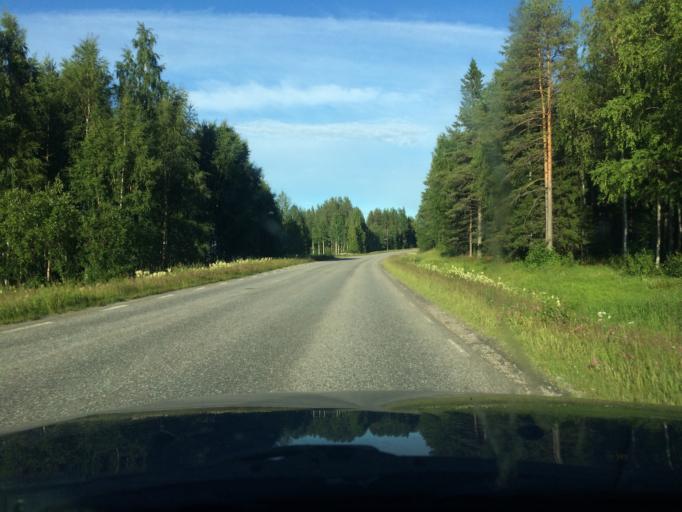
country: SE
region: Norrbotten
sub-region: Pitea Kommun
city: Roknas
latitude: 65.3193
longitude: 21.2753
